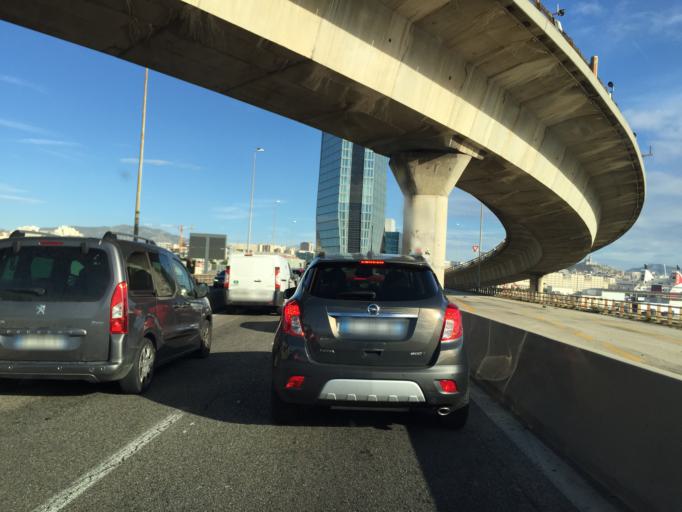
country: FR
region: Provence-Alpes-Cote d'Azur
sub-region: Departement des Bouches-du-Rhone
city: Marseille 03
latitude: 43.3174
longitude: 5.3638
